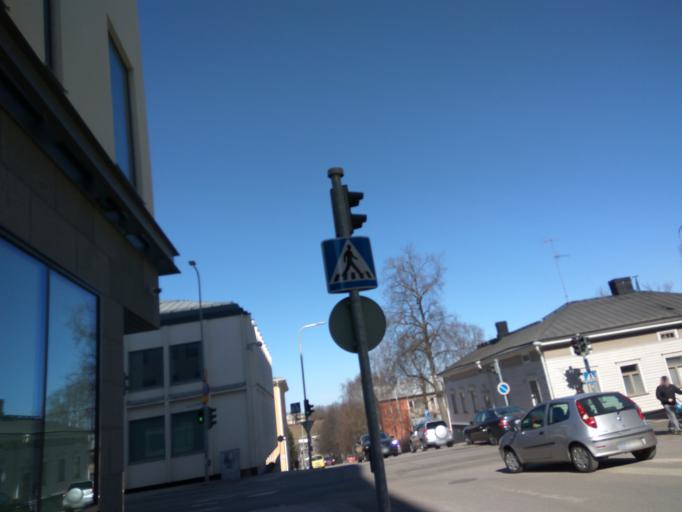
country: FI
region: South Karelia
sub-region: Lappeenranta
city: Lappeenranta
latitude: 61.0593
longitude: 28.1882
